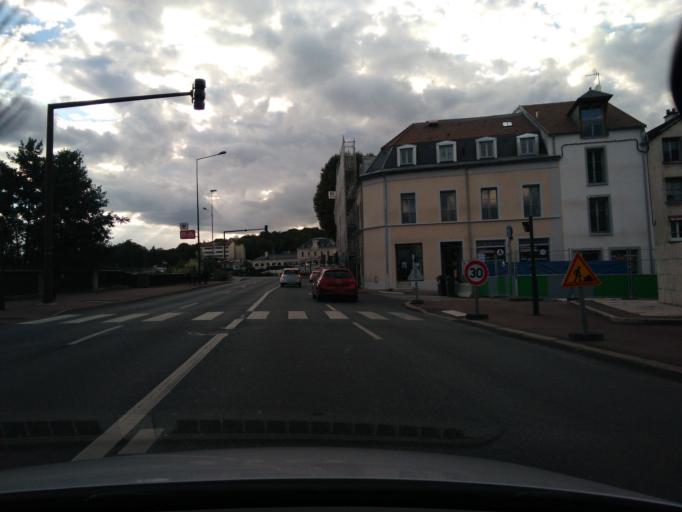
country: FR
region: Ile-de-France
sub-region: Departement de Seine-et-Marne
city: Meaux
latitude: 48.9579
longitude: 2.8776
